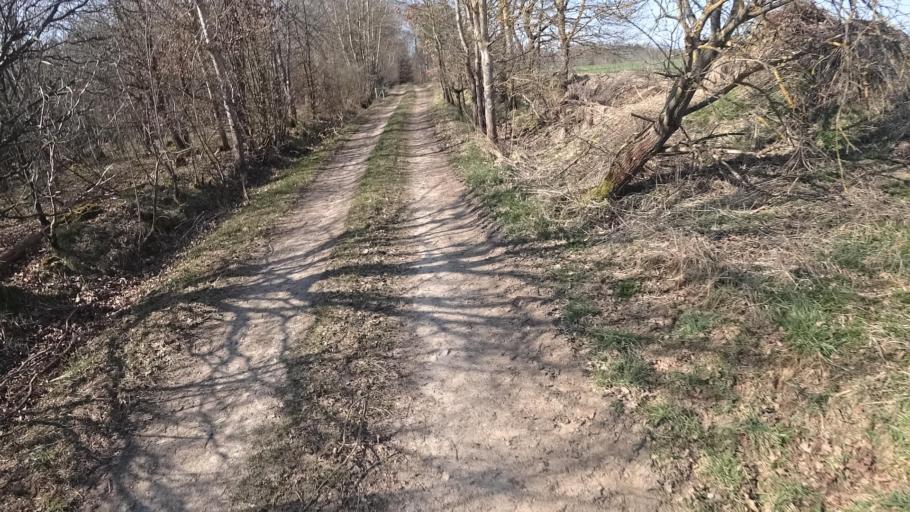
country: DE
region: Rheinland-Pfalz
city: Rheinbollen
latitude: 50.0203
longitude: 7.6599
